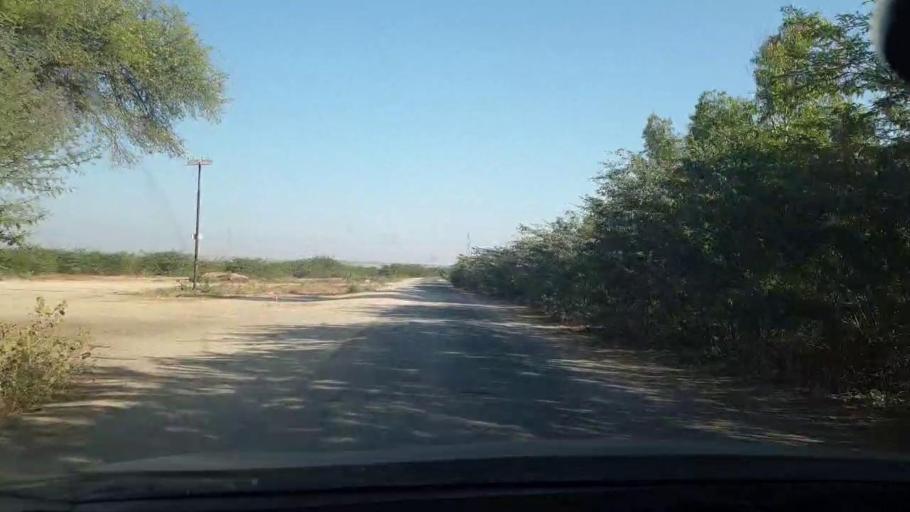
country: PK
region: Sindh
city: Malir Cantonment
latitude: 25.1538
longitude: 67.1907
